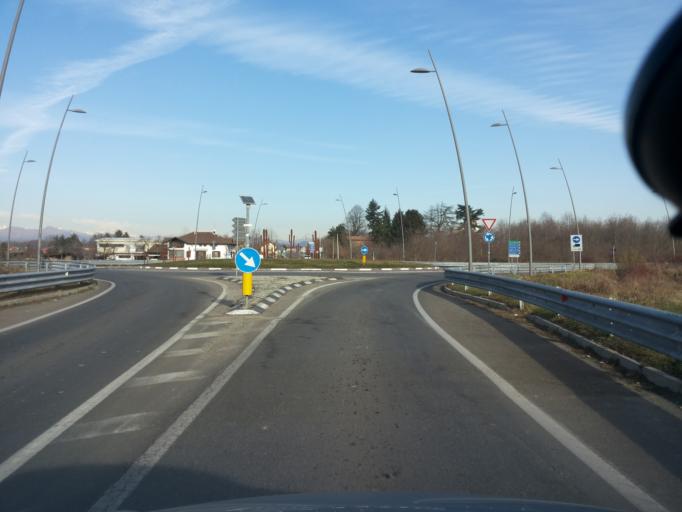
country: IT
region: Piedmont
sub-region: Provincia di Vercelli
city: Ghislarengo
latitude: 45.5220
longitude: 8.3864
